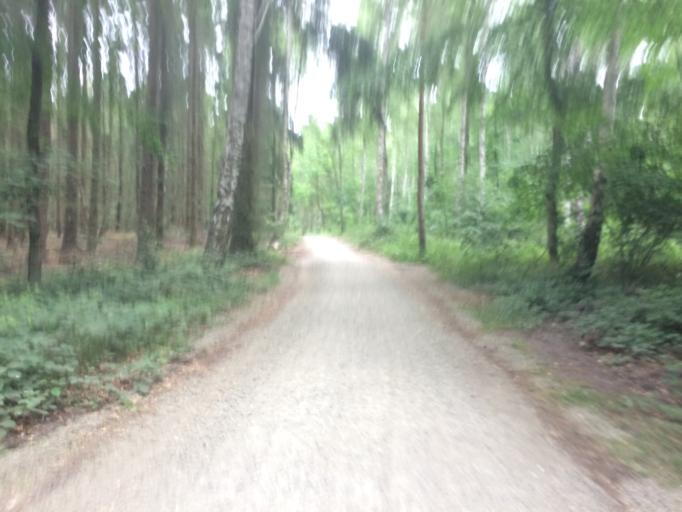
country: DK
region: Capital Region
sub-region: Bornholm Kommune
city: Ronne
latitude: 55.1259
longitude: 14.7114
